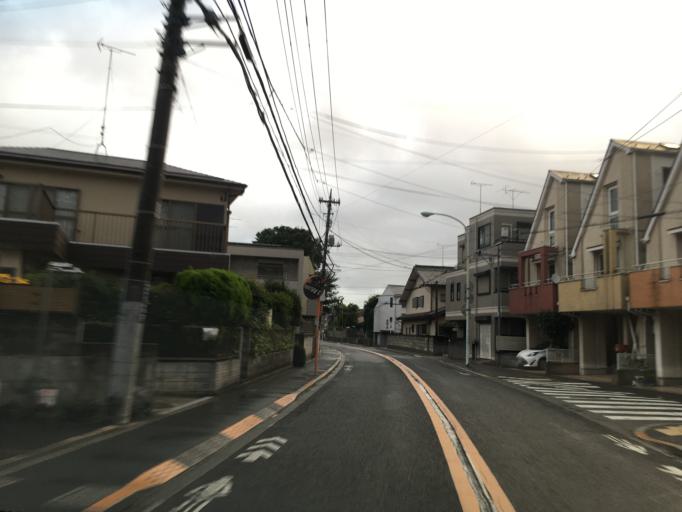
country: JP
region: Tokyo
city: Kokubunji
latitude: 35.6920
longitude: 139.5034
